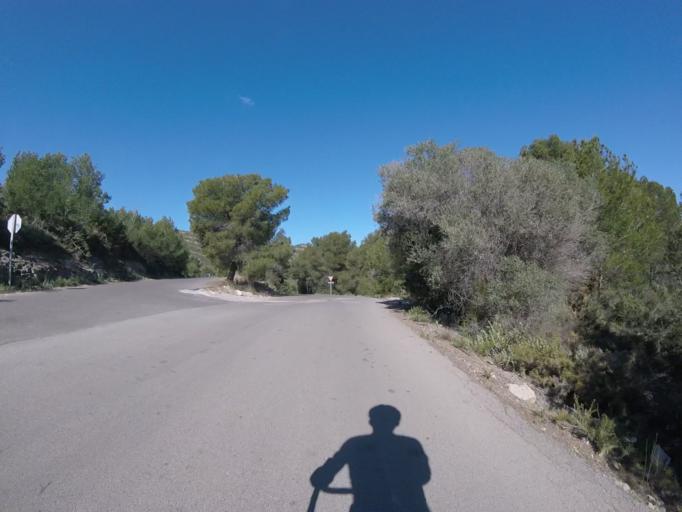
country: ES
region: Valencia
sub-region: Provincia de Castello
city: Orpesa/Oropesa del Mar
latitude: 40.0737
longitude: 0.1128
